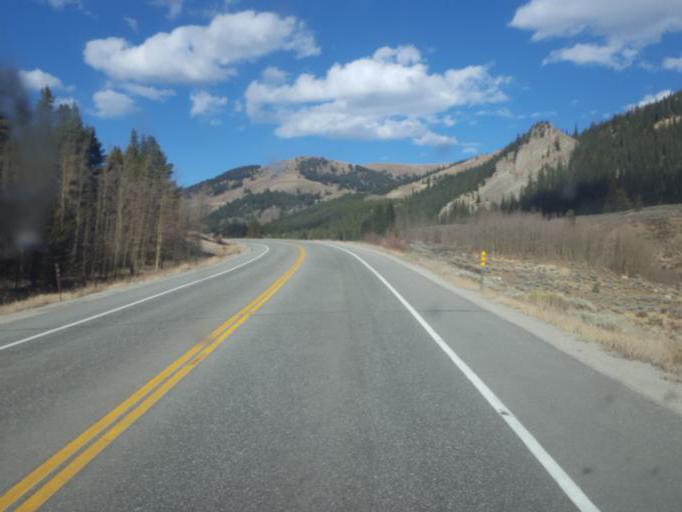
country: US
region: Colorado
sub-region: Lake County
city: Leadville
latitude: 39.3180
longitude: -106.2228
